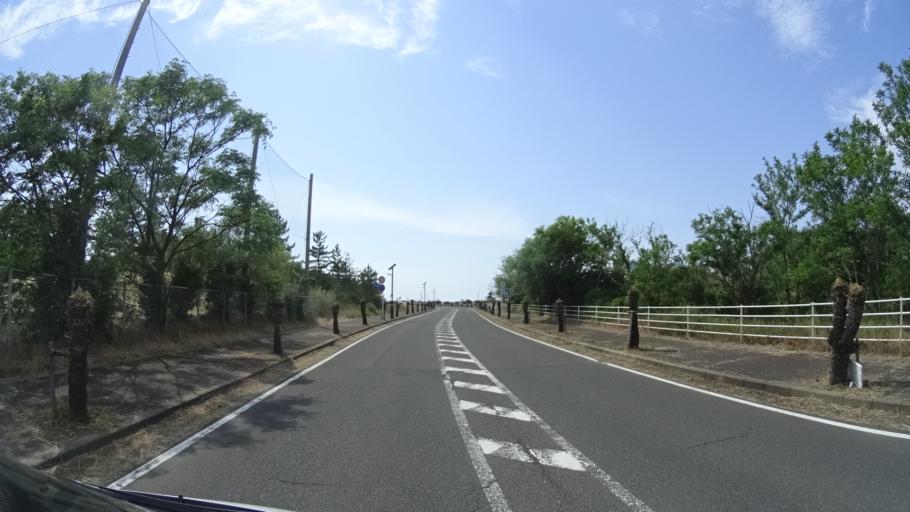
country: JP
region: Kyoto
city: Miyazu
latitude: 35.6899
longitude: 135.0321
